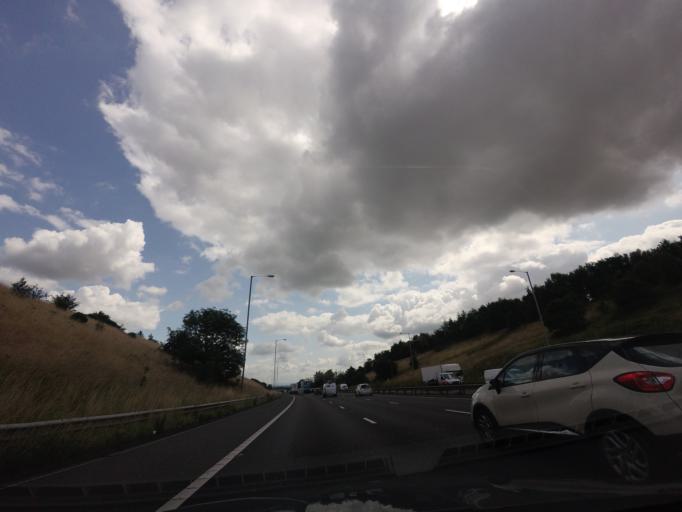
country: GB
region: England
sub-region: St. Helens
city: Billinge
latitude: 53.5130
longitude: -2.6865
